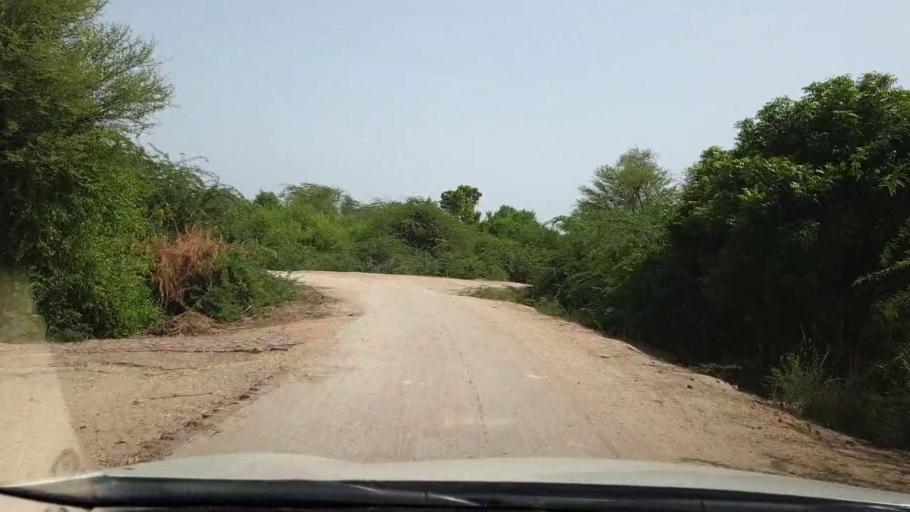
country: PK
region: Sindh
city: Tando Ghulam Ali
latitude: 25.2303
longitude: 68.9162
